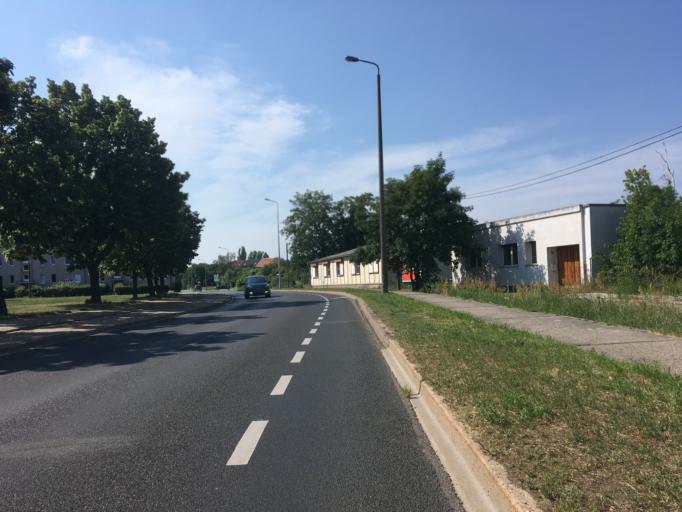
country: DE
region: Saxony-Anhalt
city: Dessau
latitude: 51.8244
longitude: 12.2351
